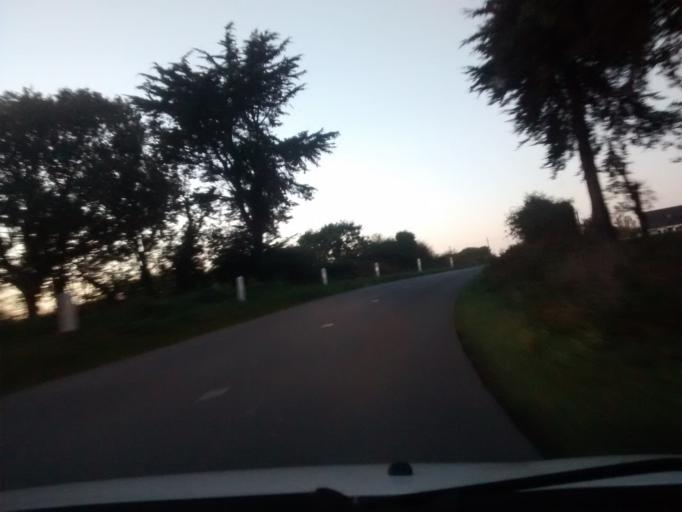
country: FR
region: Brittany
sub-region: Departement des Cotes-d'Armor
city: Trevou-Treguignec
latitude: 48.8077
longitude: -3.3286
